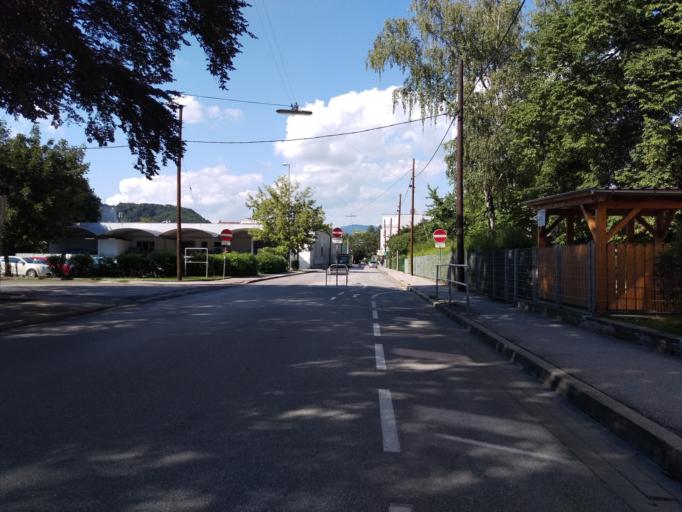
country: AT
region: Styria
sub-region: Graz Stadt
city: Wetzelsdorf
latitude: 47.0685
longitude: 15.4030
